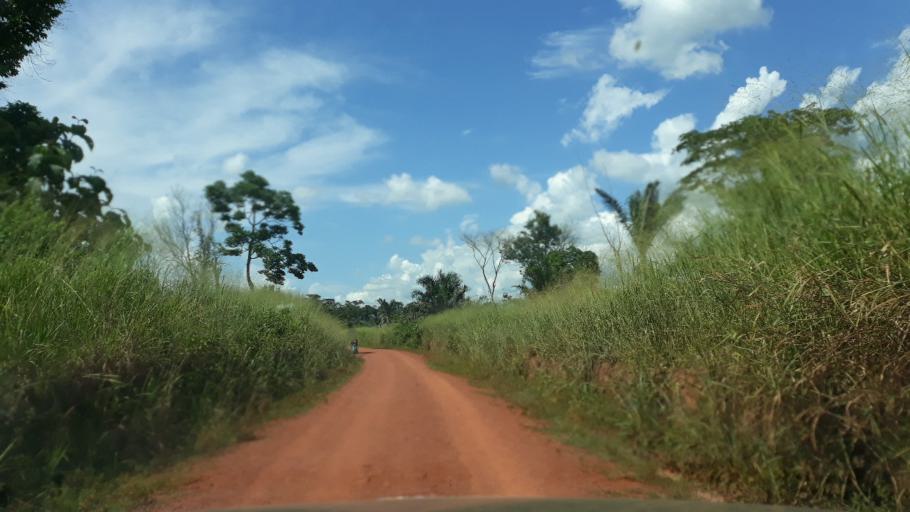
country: CD
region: Equateur
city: Businga
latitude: 3.4055
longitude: 20.3903
